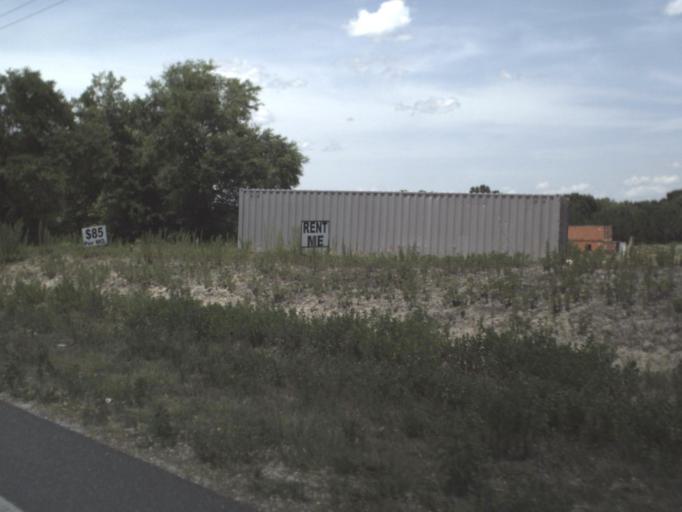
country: US
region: Florida
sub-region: Gilchrist County
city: Trenton
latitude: 29.7827
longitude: -82.8667
